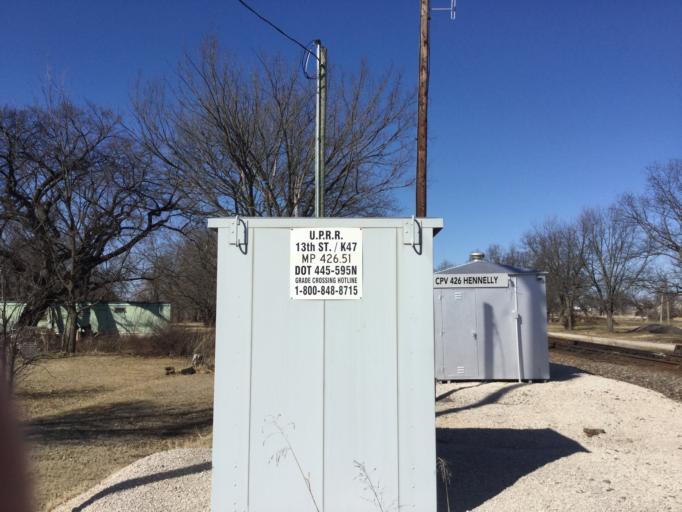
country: US
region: Kansas
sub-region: Wilson County
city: Neodesha
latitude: 37.5301
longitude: -95.6612
